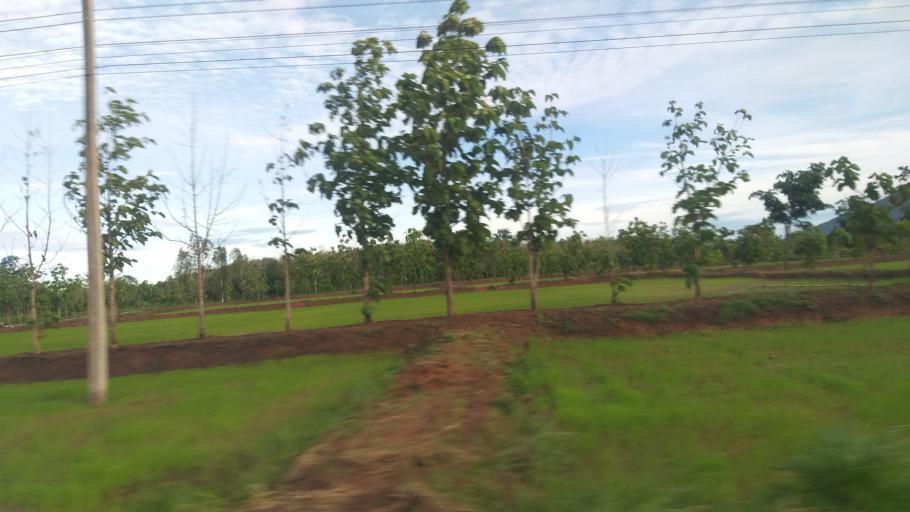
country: TH
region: Chaiyaphum
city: Phu Khiao
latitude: 16.3442
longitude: 102.2387
